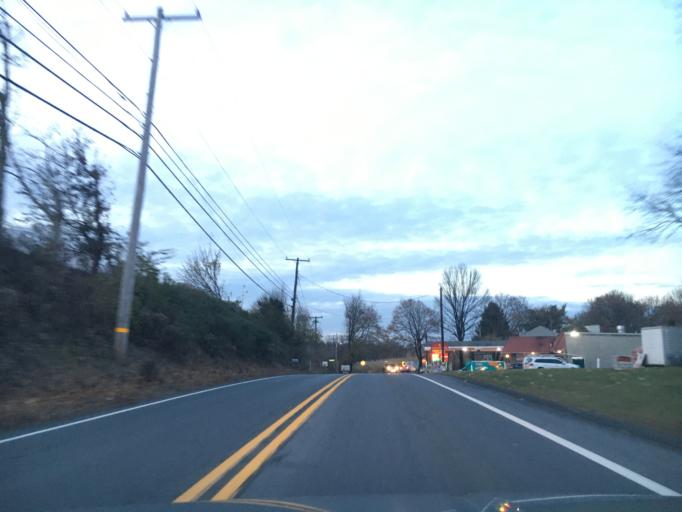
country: US
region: Pennsylvania
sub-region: Lehigh County
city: Schnecksville
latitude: 40.6775
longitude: -75.5704
